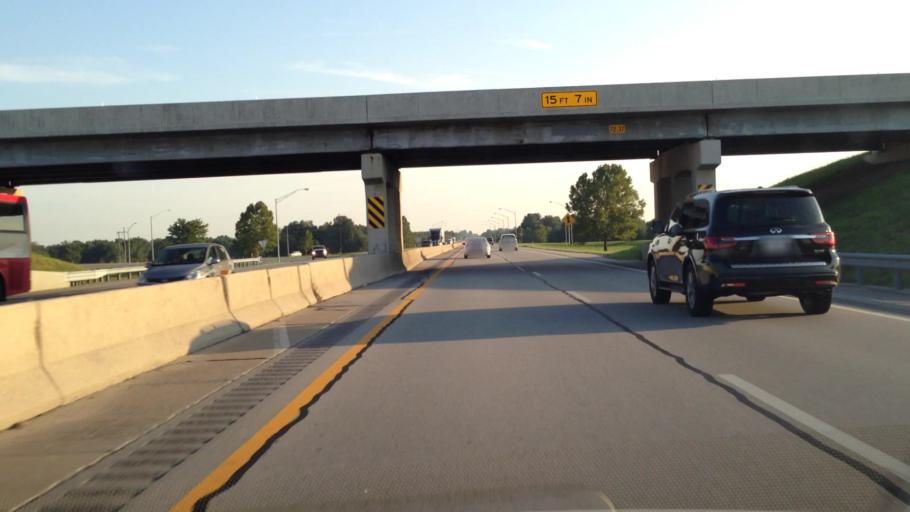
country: US
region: Oklahoma
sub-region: Ottawa County
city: Miami
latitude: 36.8659
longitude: -94.8497
